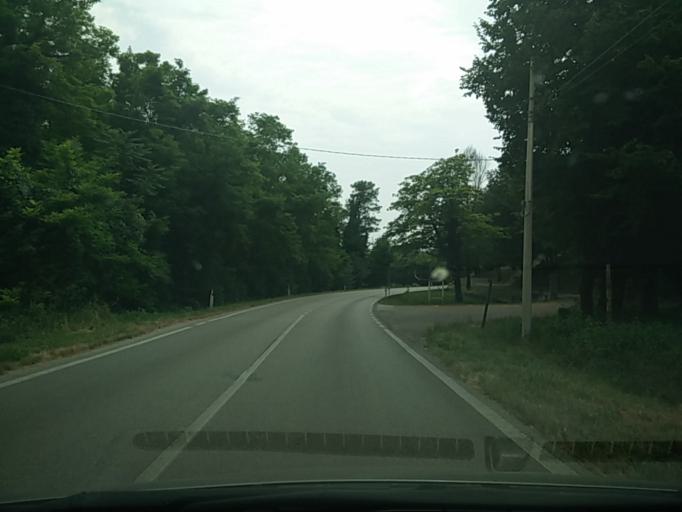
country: IT
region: Friuli Venezia Giulia
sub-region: Provincia di Pordenone
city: Aviano-Castello
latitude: 46.0730
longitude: 12.5765
